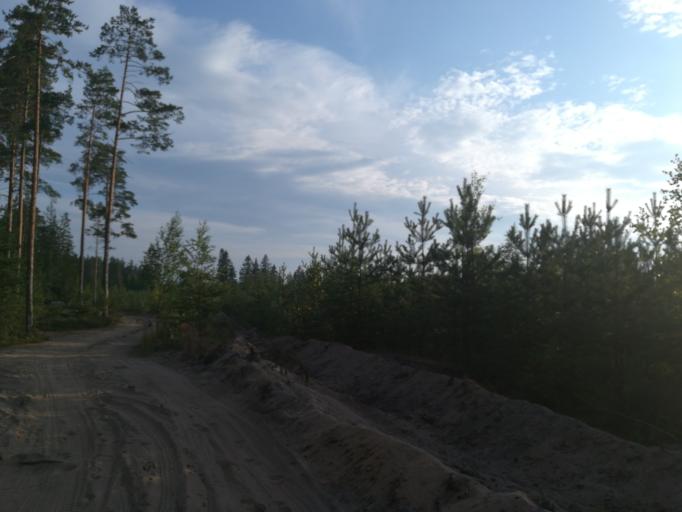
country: RU
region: Leningrad
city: Ust'-Luga
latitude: 59.6790
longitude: 28.2284
